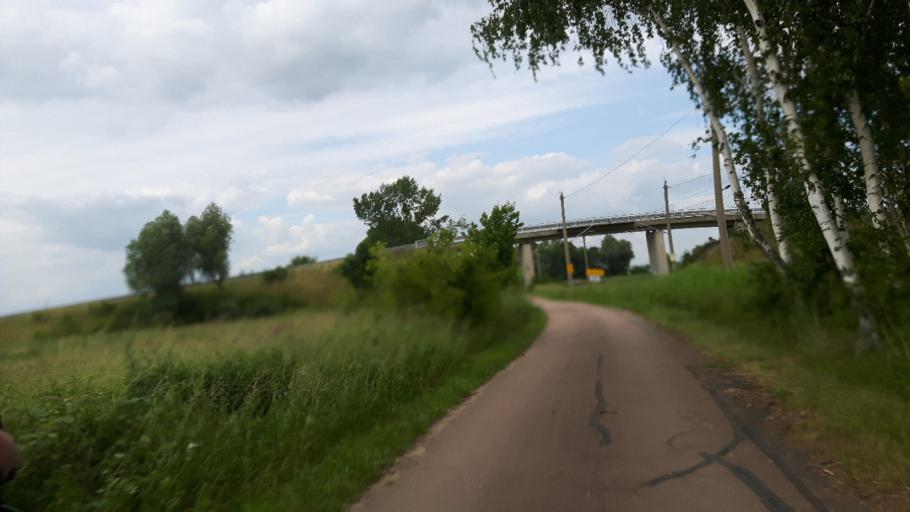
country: DE
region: Saxony-Anhalt
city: Bergwitz
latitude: 51.8273
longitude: 12.6108
